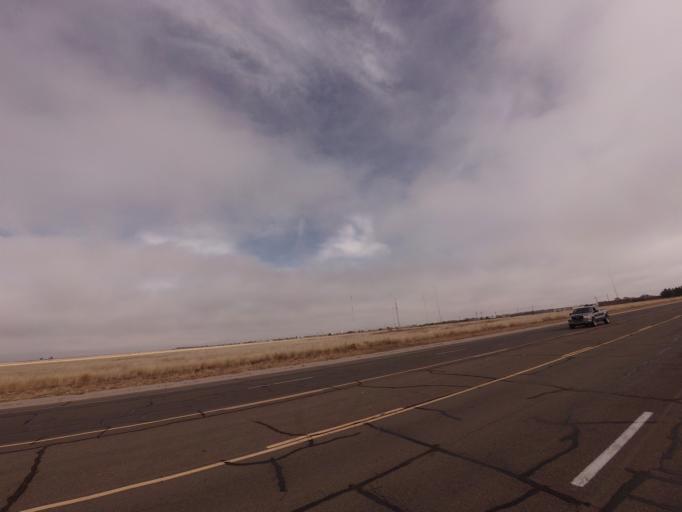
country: US
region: New Mexico
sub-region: Curry County
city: Clovis
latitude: 34.4340
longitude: -103.2179
